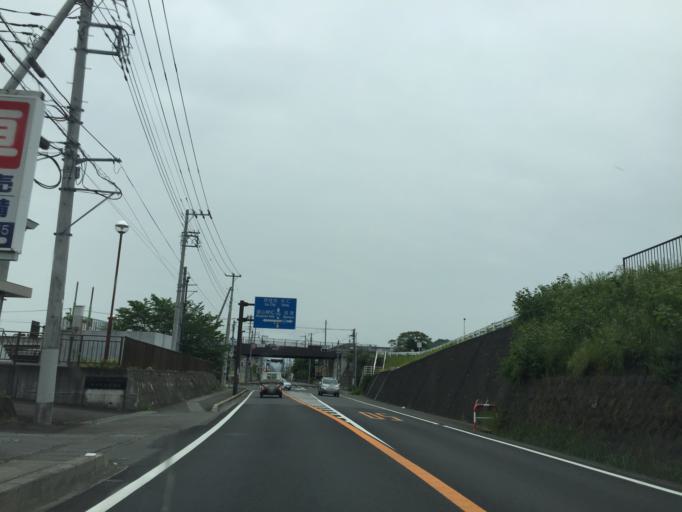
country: JP
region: Shizuoka
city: Mishima
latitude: 35.0568
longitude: 138.9411
